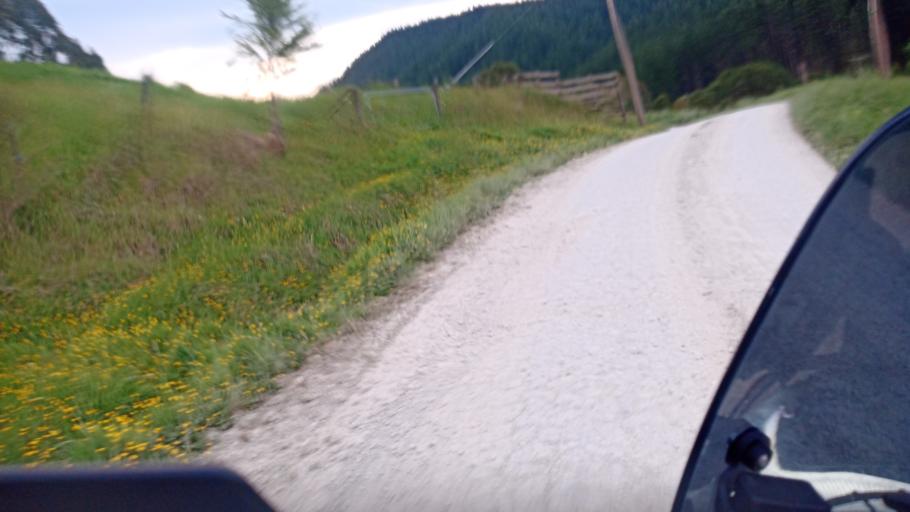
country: NZ
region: Gisborne
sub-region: Gisborne District
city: Gisborne
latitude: -38.4657
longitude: 177.9714
